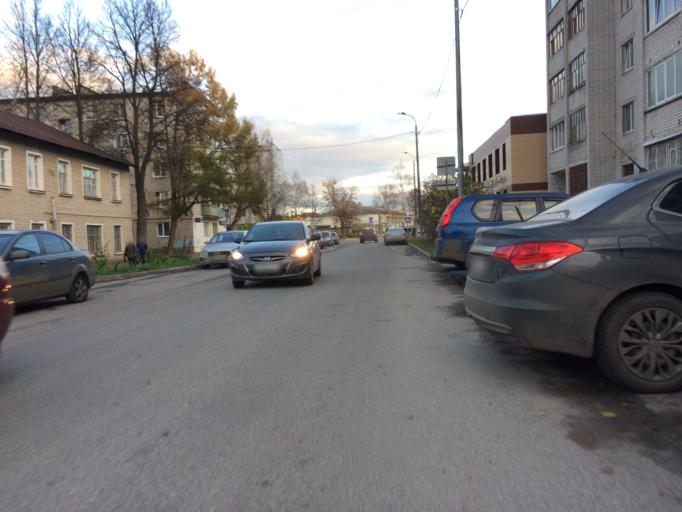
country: RU
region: Mariy-El
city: Yoshkar-Ola
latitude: 56.6468
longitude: 47.8988
